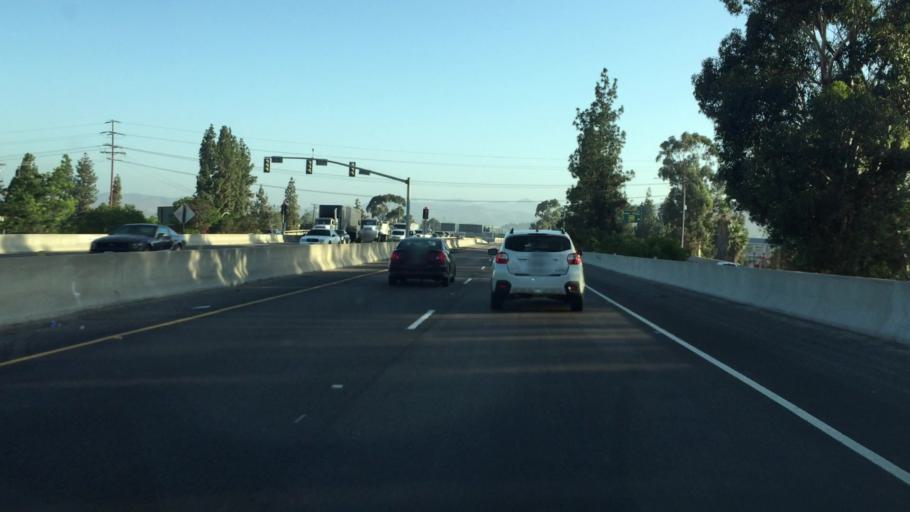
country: US
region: California
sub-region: San Diego County
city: El Cajon
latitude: 32.8064
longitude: -116.9620
